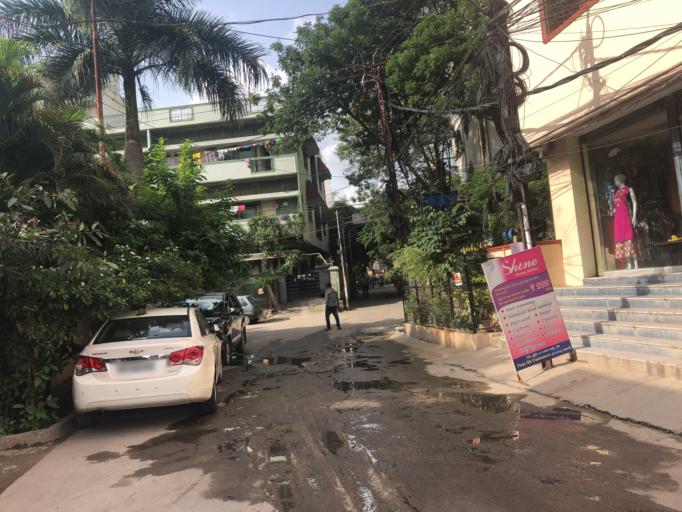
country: IN
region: Telangana
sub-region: Rangareddi
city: Kukatpalli
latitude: 17.4394
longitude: 78.4388
